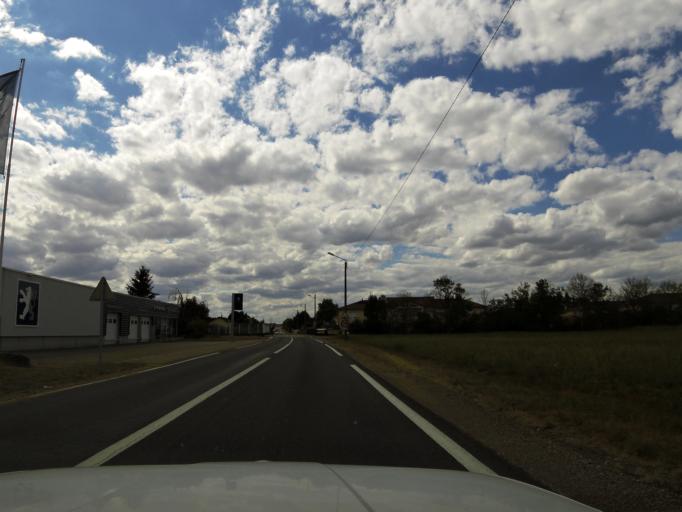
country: FR
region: Rhone-Alpes
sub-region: Departement de l'Ain
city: Loyettes
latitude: 45.7807
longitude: 5.2142
